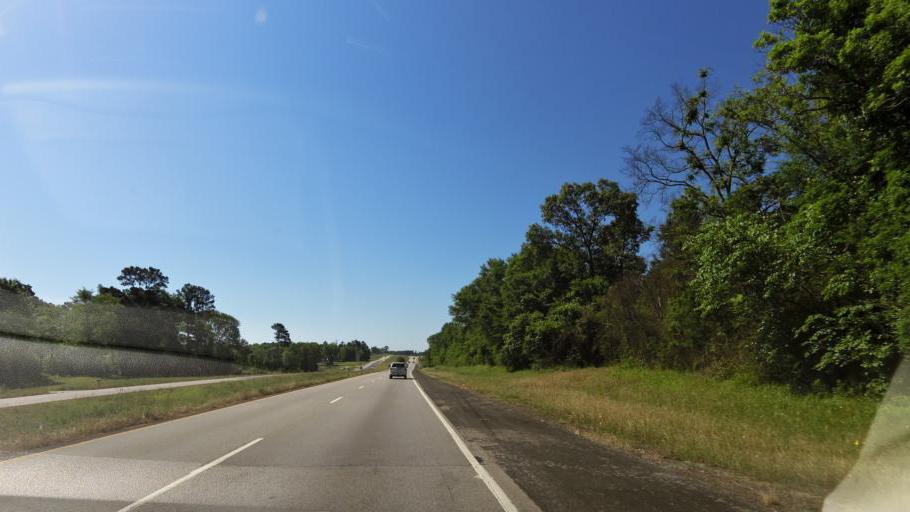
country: US
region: Texas
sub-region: Angelina County
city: Redland
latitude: 31.4234
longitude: -94.7246
